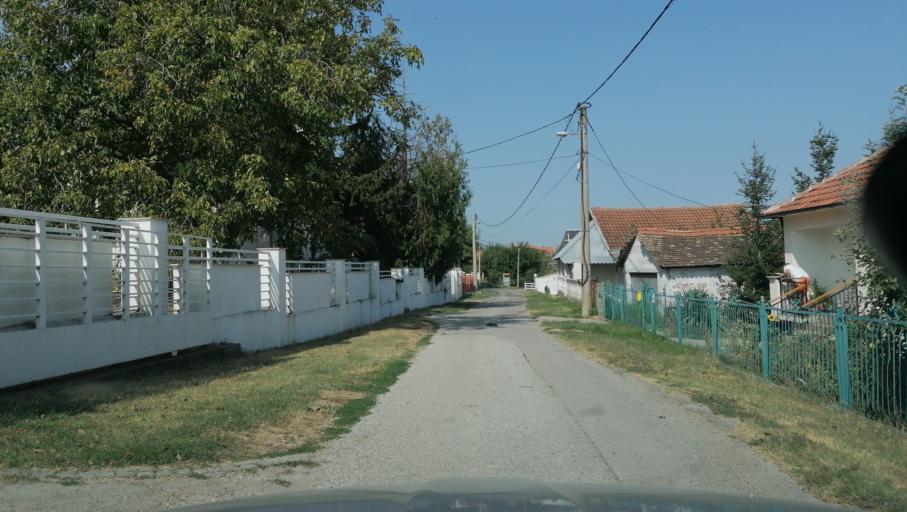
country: RS
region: Central Serbia
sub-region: Belgrade
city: Zvezdara
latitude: 44.6907
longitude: 20.5552
